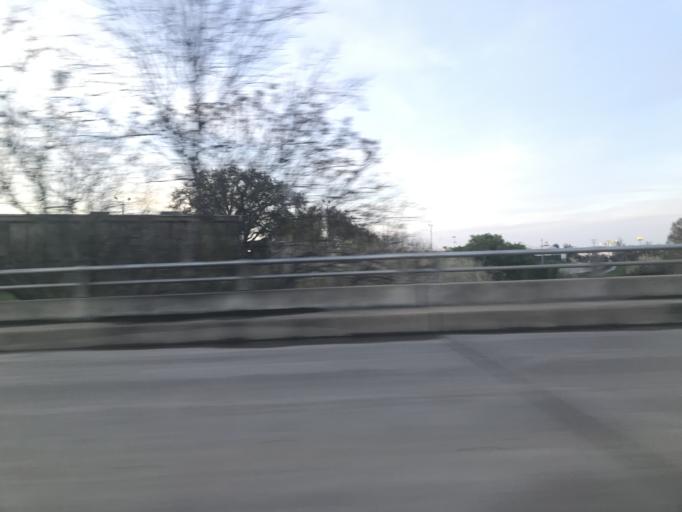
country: US
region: Texas
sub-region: Tom Green County
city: San Angelo
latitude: 31.4603
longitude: -100.4496
